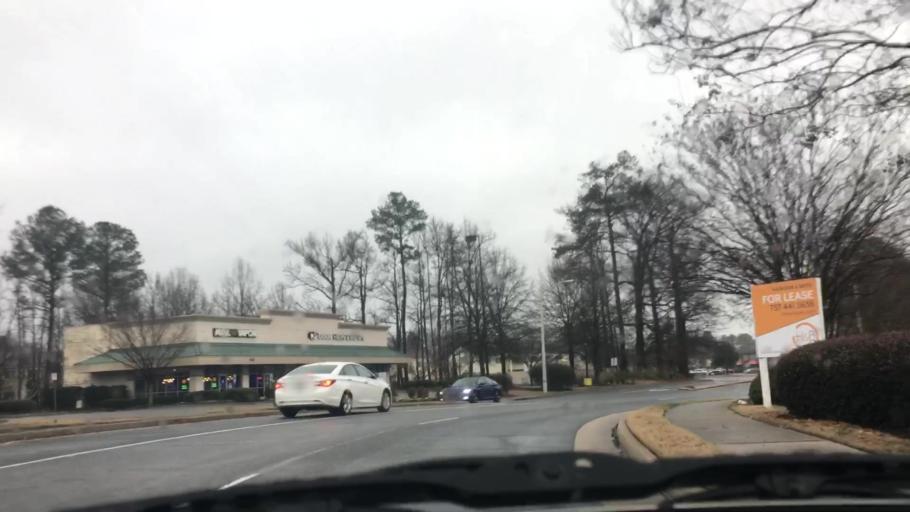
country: US
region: Virginia
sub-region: City of Chesapeake
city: Chesapeake
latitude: 36.7678
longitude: -76.2489
